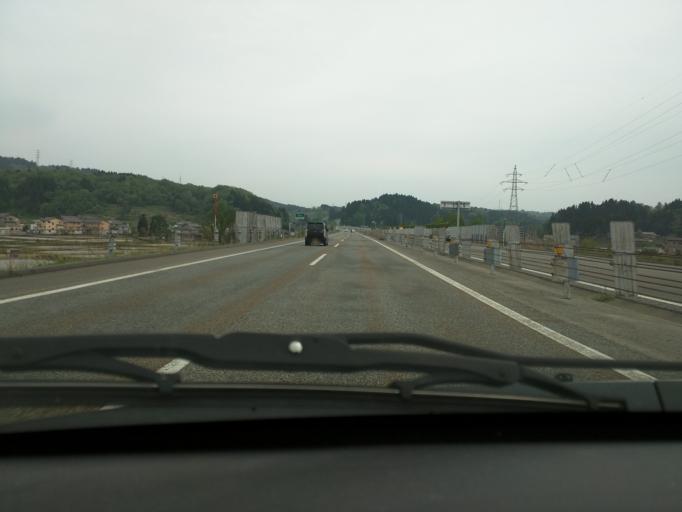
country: JP
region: Niigata
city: Ojiya
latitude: 37.2910
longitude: 138.7836
